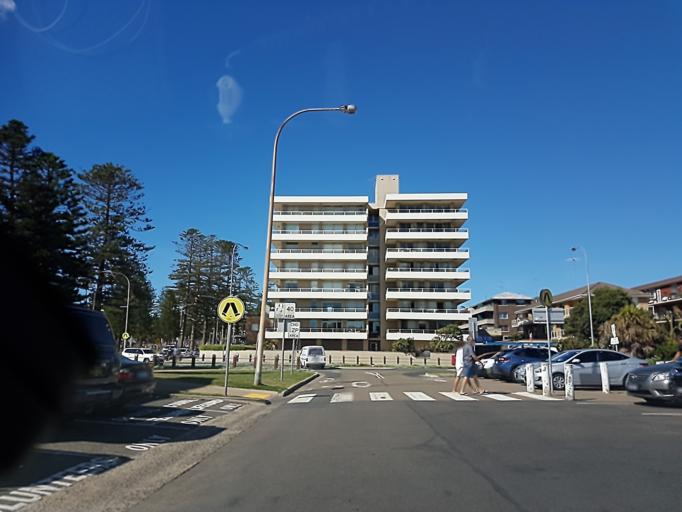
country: AU
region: New South Wales
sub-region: Warringah
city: Dee Why
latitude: -33.7522
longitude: 151.2965
